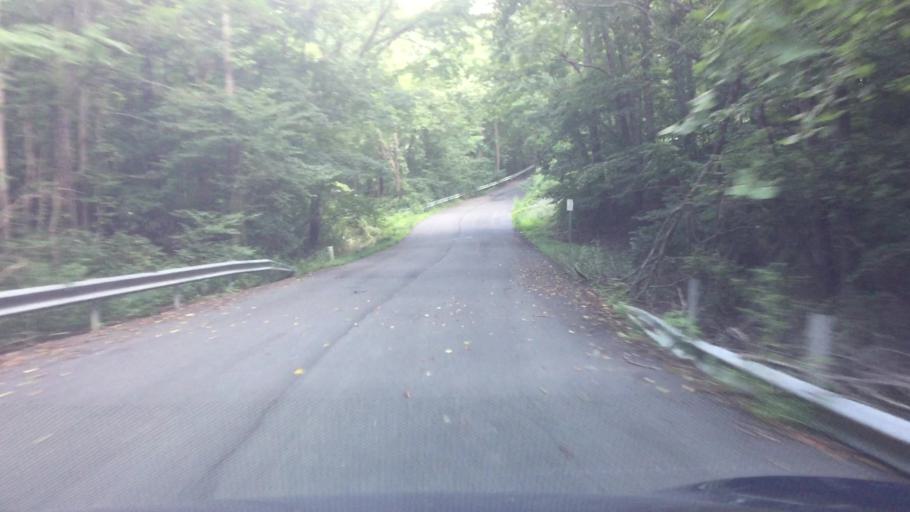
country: US
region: Virginia
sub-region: Wythe County
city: Wytheville
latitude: 36.9458
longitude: -81.0516
